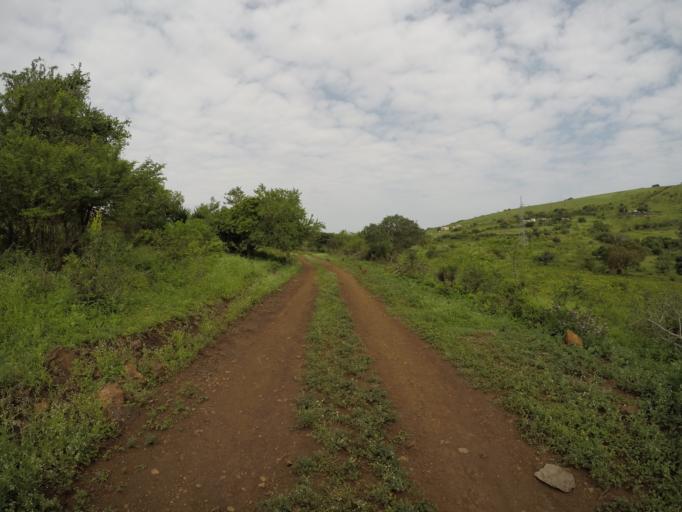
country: ZA
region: KwaZulu-Natal
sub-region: uThungulu District Municipality
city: Empangeni
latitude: -28.6282
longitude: 31.9068
